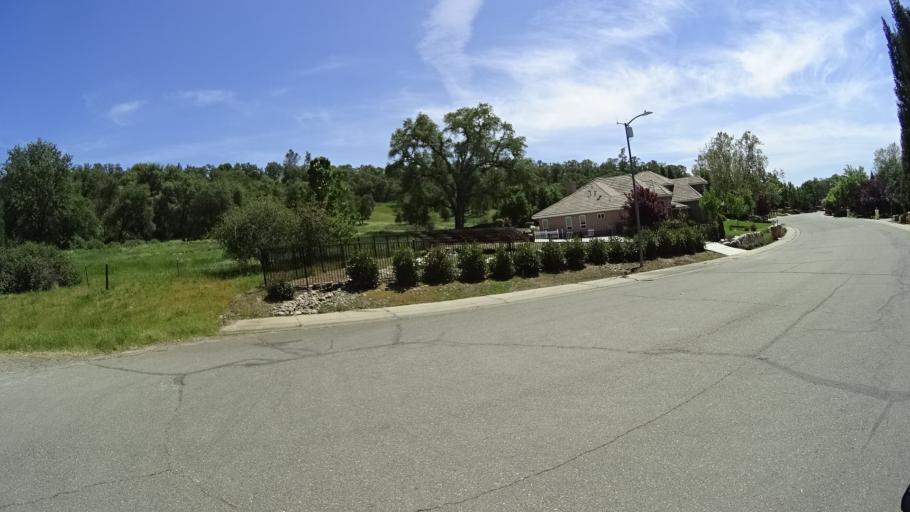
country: US
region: California
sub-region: Placer County
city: Rocklin
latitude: 38.8224
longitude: -121.2289
